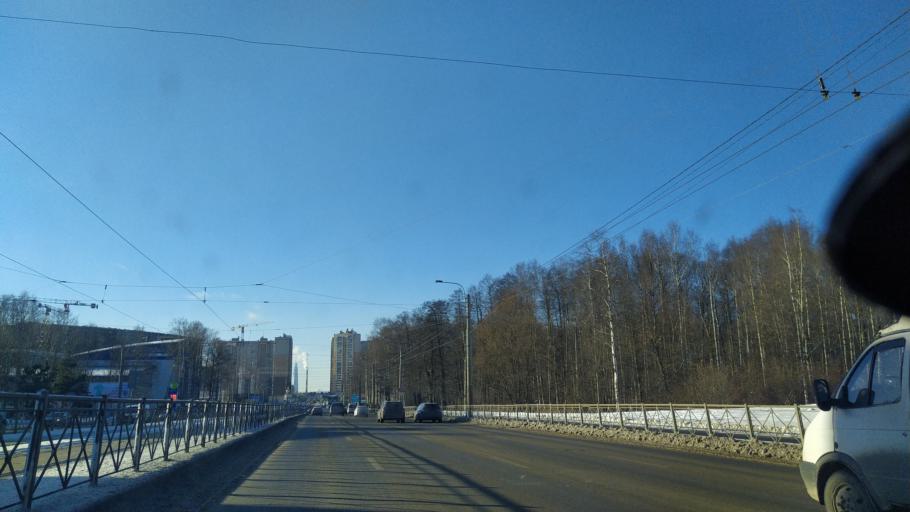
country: RU
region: Leningrad
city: Udel'naya
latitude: 60.0024
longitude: 30.3162
